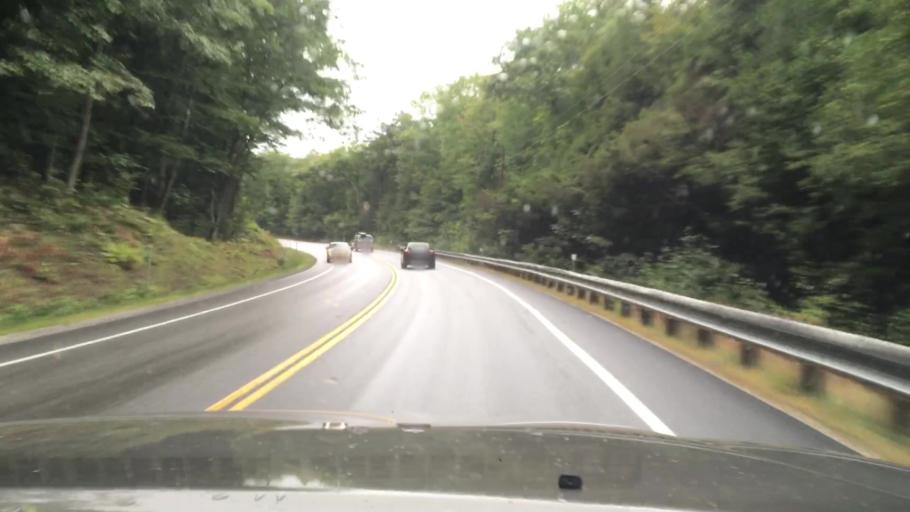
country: US
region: New Hampshire
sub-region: Hillsborough County
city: Antrim
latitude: 43.0738
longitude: -72.0385
